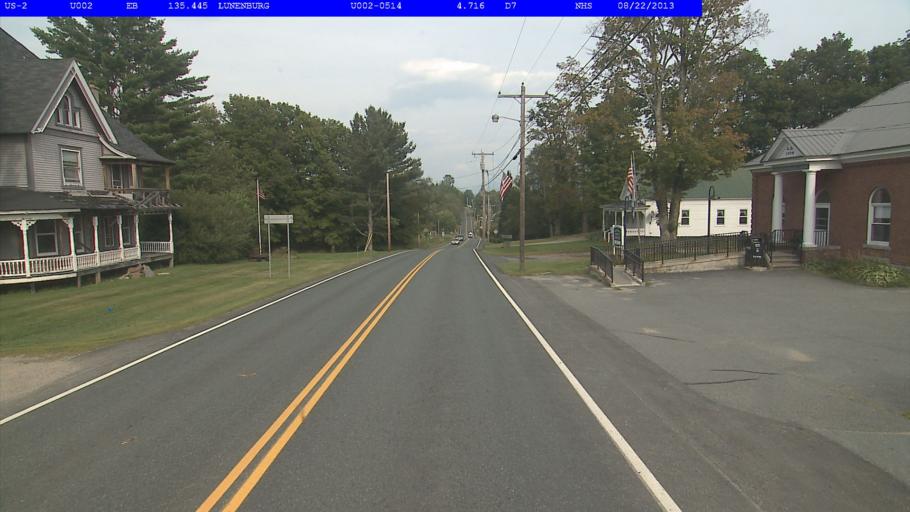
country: US
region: New Hampshire
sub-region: Coos County
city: Whitefield
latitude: 44.4632
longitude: -71.6819
